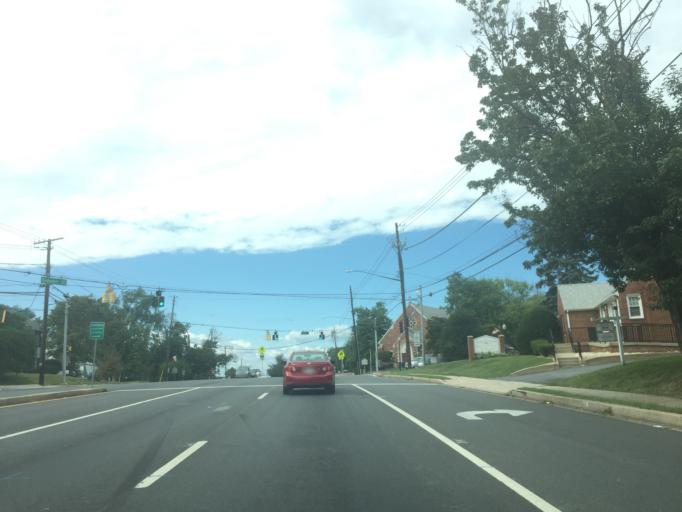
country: US
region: Maryland
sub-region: Montgomery County
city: Gaithersburg
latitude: 39.1375
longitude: -77.1936
